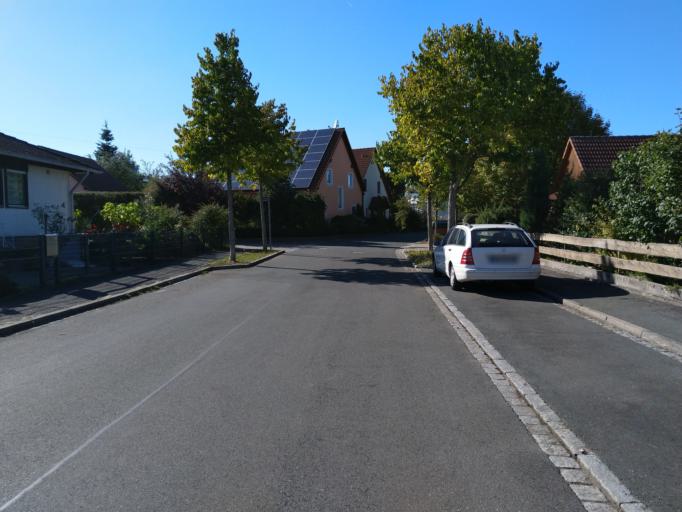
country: DE
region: Bavaria
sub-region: Regierungsbezirk Mittelfranken
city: Hagenbuchach
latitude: 49.5345
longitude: 10.7665
